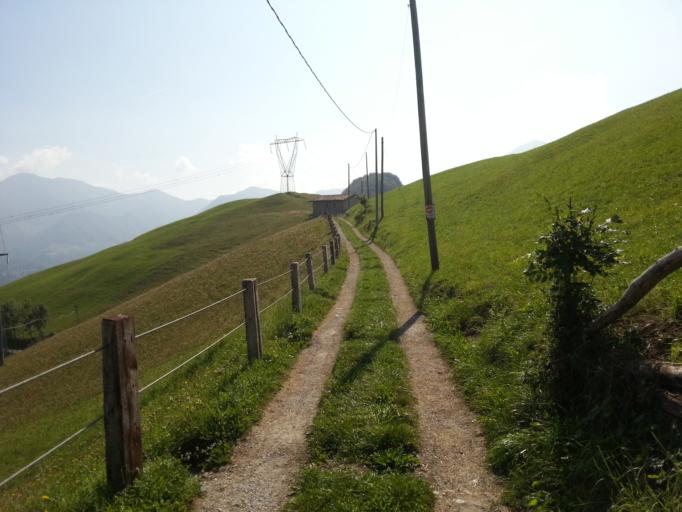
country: IT
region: Lombardy
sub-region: Provincia di Lecco
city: Pasturo
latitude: 45.9447
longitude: 9.4304
